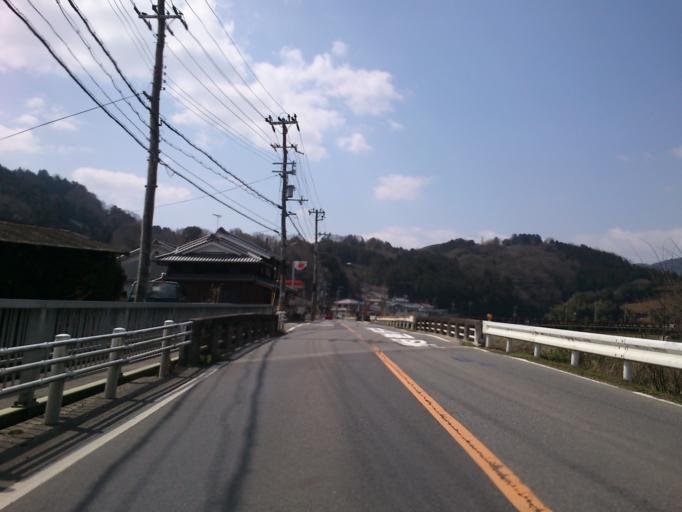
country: JP
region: Kyoto
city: Tanabe
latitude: 34.7910
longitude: 135.8967
